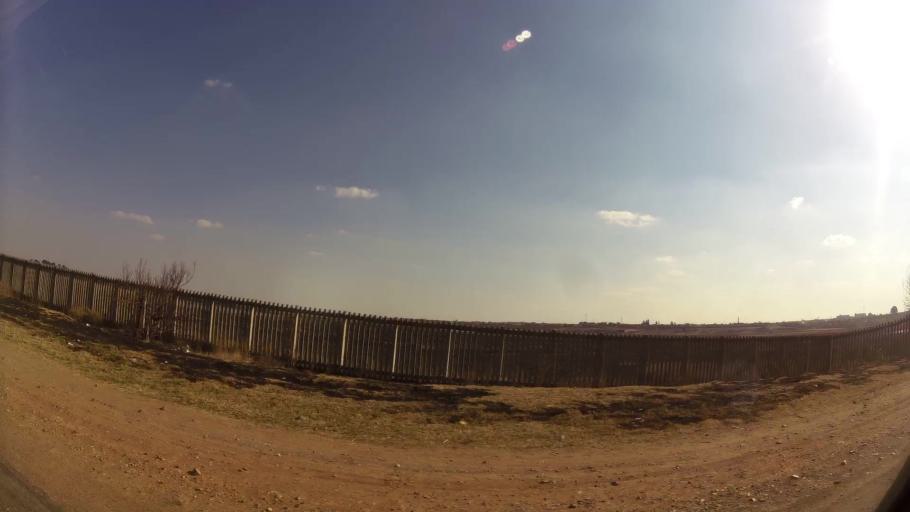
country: ZA
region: Gauteng
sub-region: Ekurhuleni Metropolitan Municipality
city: Benoni
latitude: -26.2281
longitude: 28.3212
